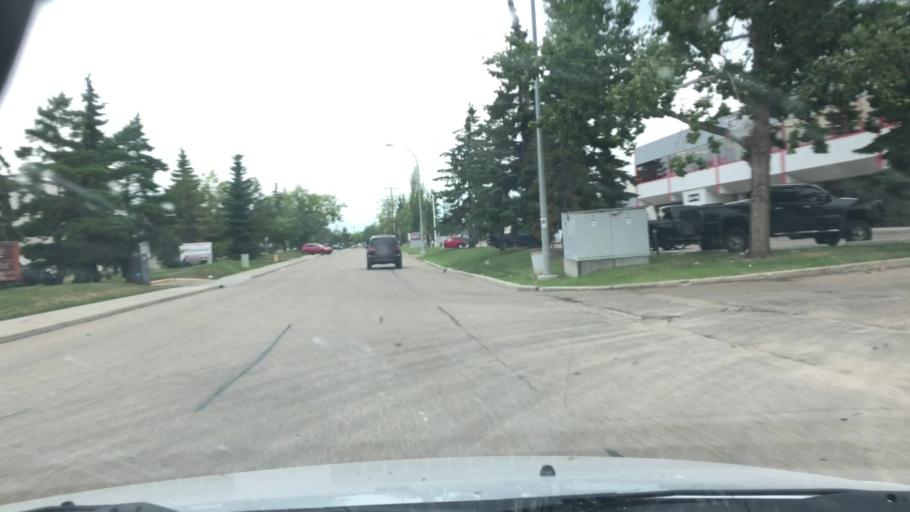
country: CA
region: Alberta
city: Edmonton
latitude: 53.5318
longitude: -113.4149
